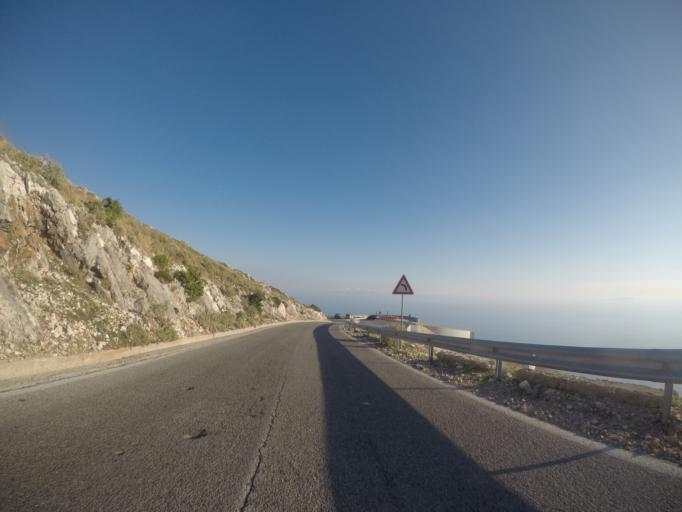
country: AL
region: Vlore
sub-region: Rrethi i Vlores
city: Vranisht
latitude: 40.1891
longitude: 19.5990
